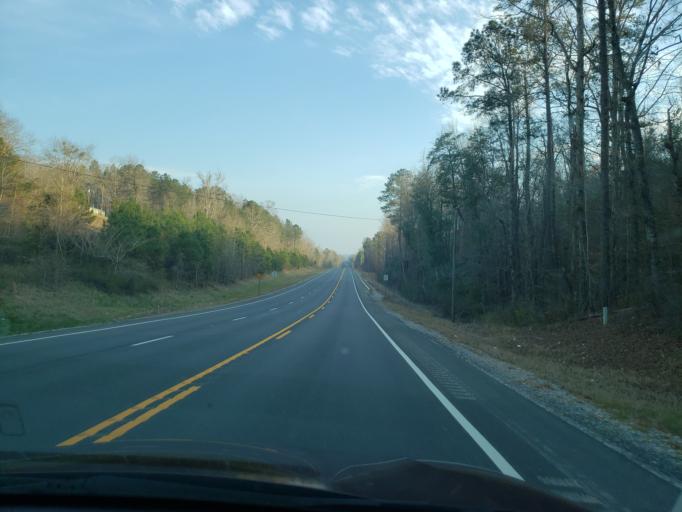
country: US
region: Alabama
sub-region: Hale County
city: Moundville
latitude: 32.8553
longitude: -87.6132
